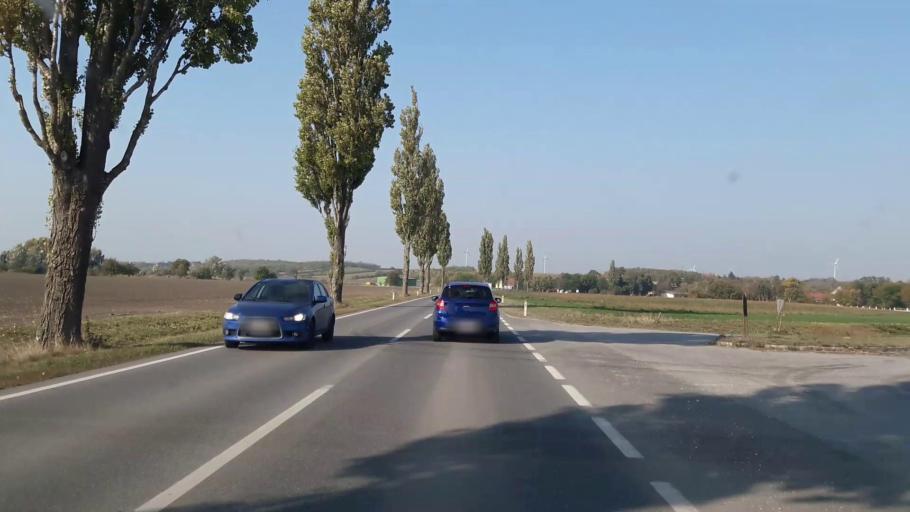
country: AT
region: Lower Austria
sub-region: Politischer Bezirk Ganserndorf
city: Engelhartstetten
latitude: 48.2139
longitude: 16.9012
